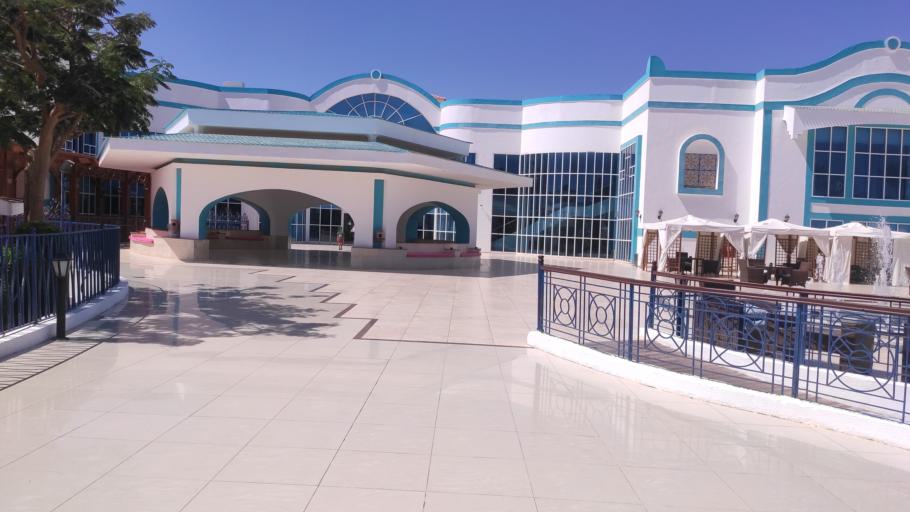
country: EG
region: South Sinai
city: Sharm el-Sheikh
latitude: 27.9443
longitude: 34.3810
